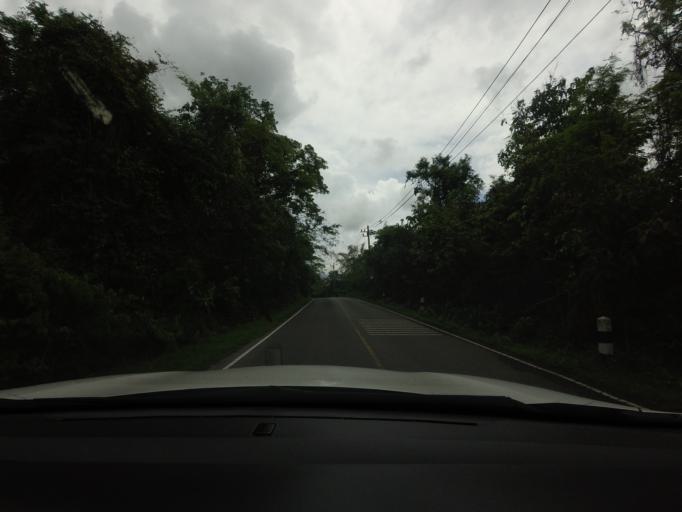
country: TH
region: Nakhon Ratchasima
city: Pak Chong
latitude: 14.4972
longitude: 101.3851
